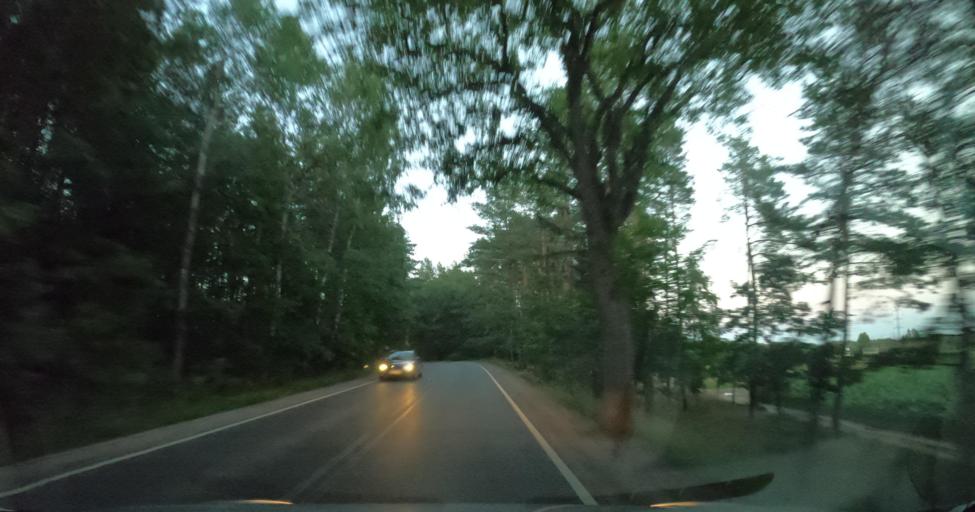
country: PL
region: Pomeranian Voivodeship
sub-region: Powiat wejherowski
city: Szemud
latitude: 54.4713
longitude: 18.1694
